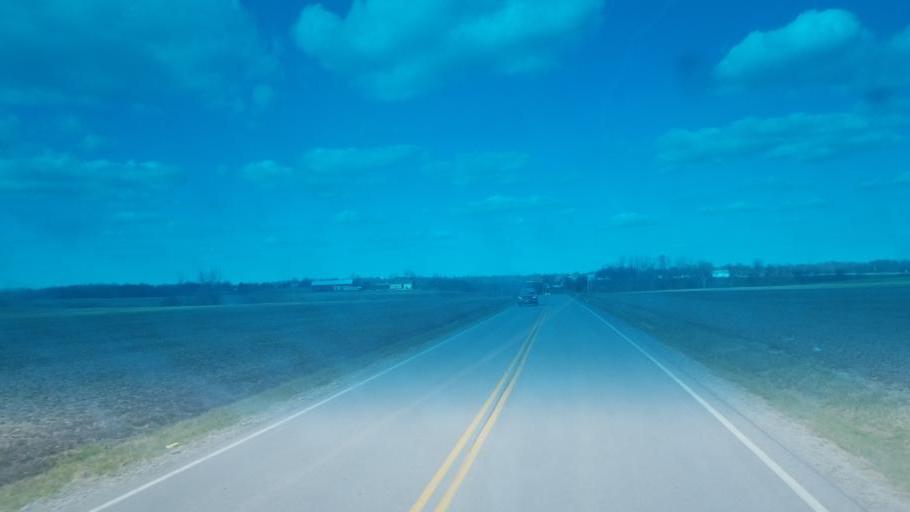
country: US
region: Ohio
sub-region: Highland County
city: Greenfield
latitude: 39.3327
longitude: -83.4080
